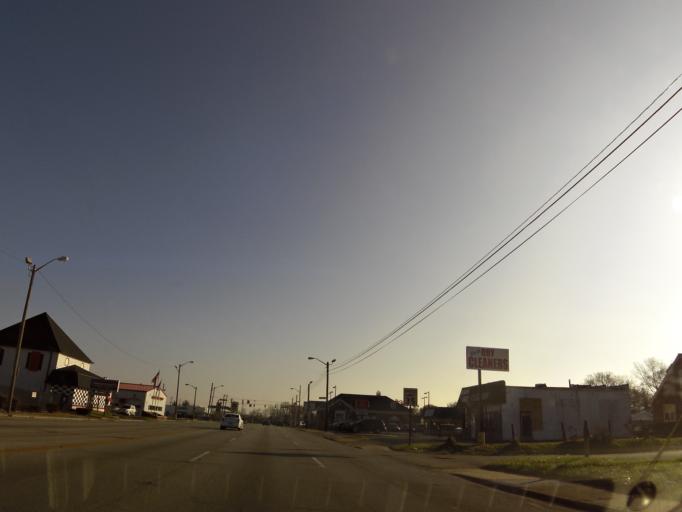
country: US
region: Indiana
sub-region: Marion County
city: Indianapolis
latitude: 39.7879
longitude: -86.2049
